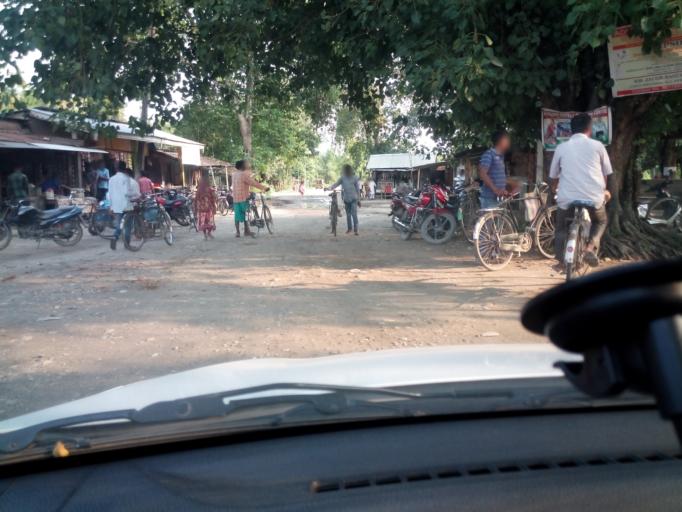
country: IN
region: Assam
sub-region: Udalguri
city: Udalguri
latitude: 26.7306
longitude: 92.0855
